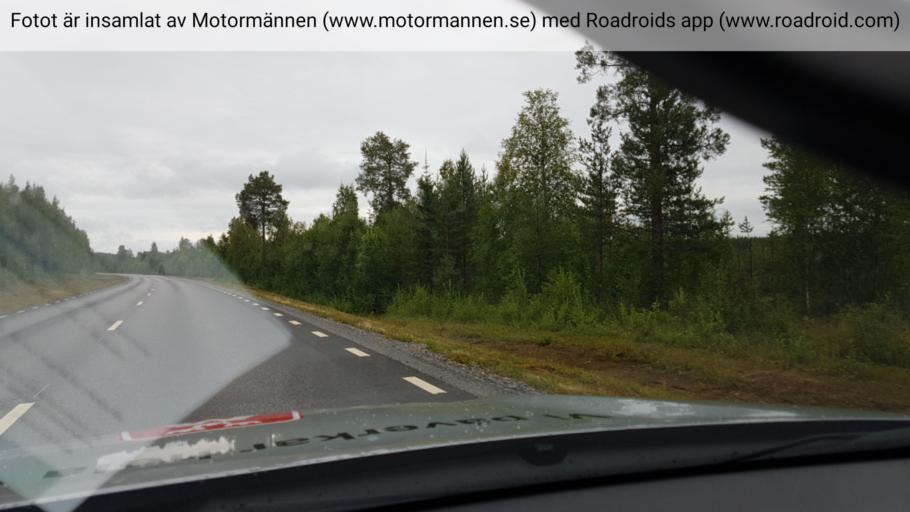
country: SE
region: Norrbotten
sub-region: Alvsbyns Kommun
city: AElvsbyn
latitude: 66.3102
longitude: 20.7977
